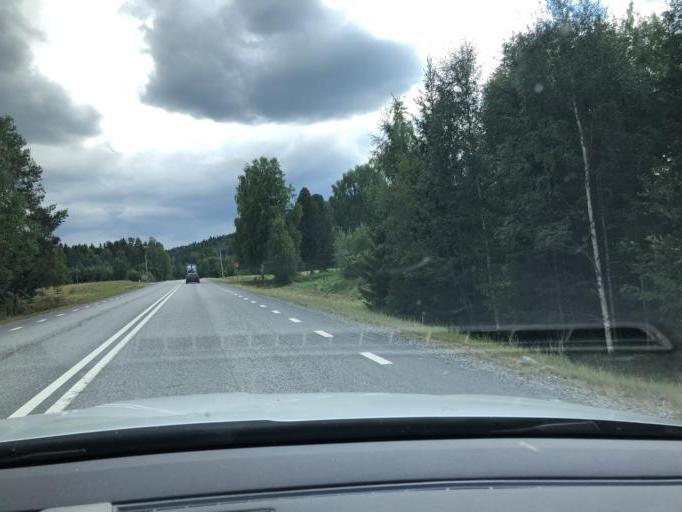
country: SE
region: Vaesternorrland
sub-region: Solleftea Kommun
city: Solleftea
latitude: 63.3112
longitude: 17.1994
